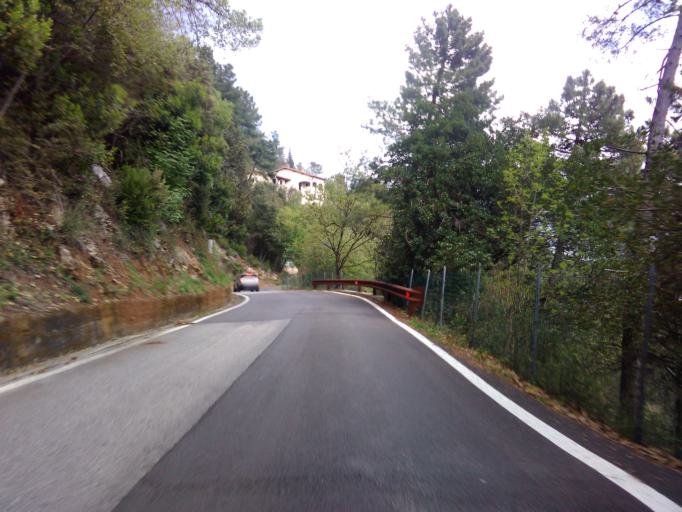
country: IT
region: Tuscany
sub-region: Provincia di Lucca
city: Pontestazzemese
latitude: 43.9560
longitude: 10.2798
